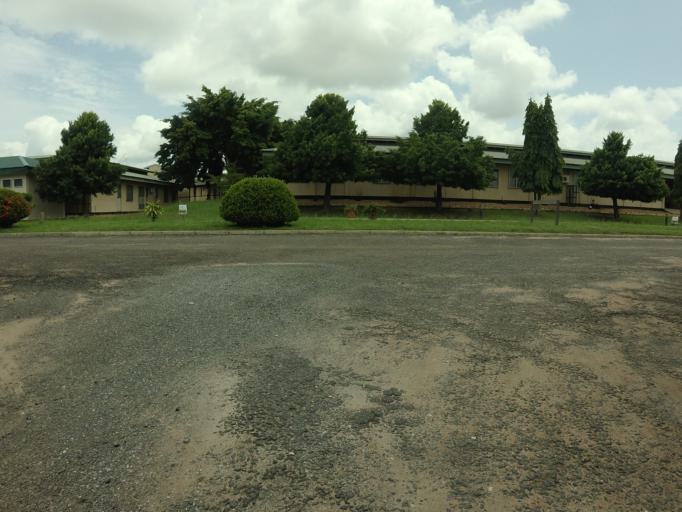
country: GH
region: Volta
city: Ho
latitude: 6.6014
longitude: 0.4847
